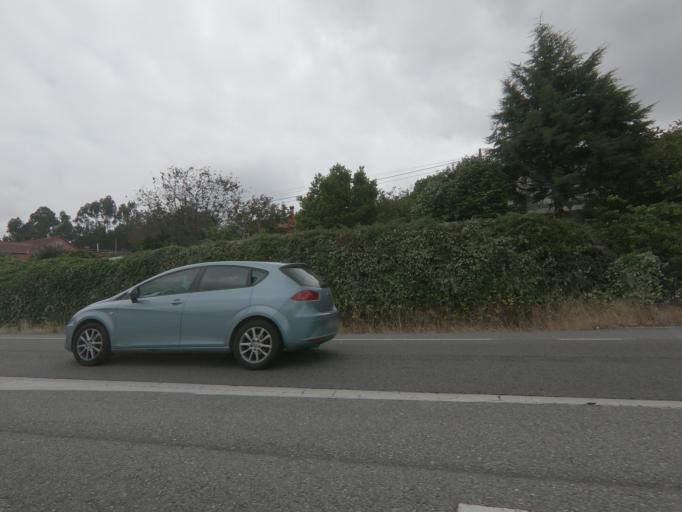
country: PT
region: Viana do Castelo
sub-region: Valenca
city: Valenca
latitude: 42.0013
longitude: -8.6857
